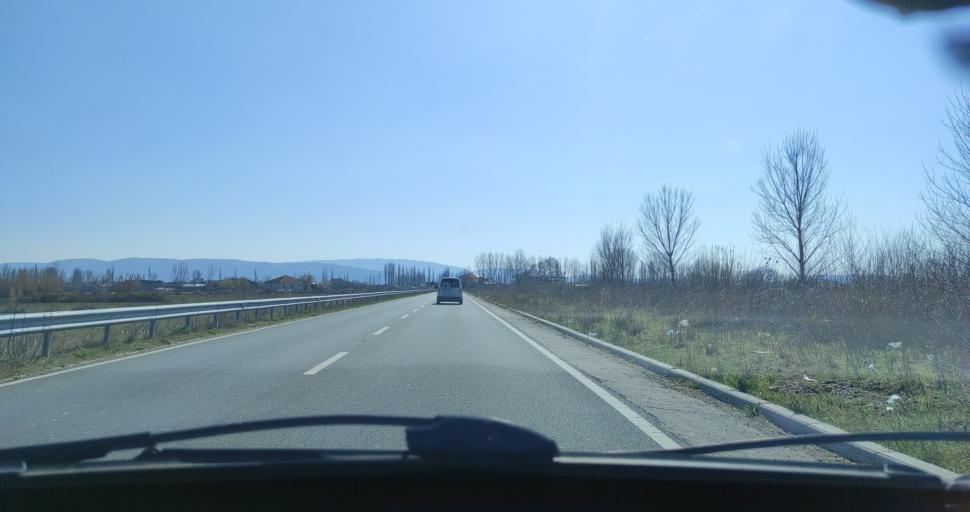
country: AL
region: Shkoder
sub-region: Rrethi i Shkodres
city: Berdica e Madhe
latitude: 41.9904
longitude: 19.4788
